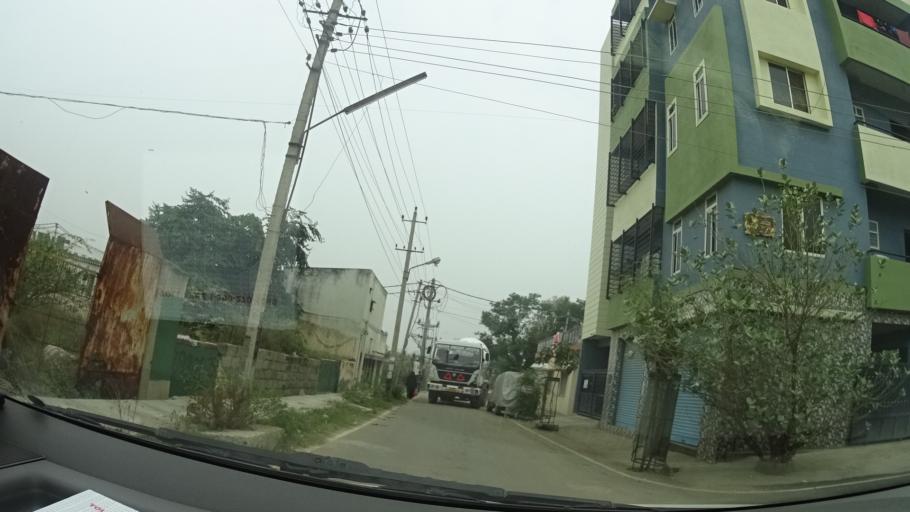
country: IN
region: Karnataka
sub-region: Bangalore Urban
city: Yelahanka
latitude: 13.0382
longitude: 77.6334
